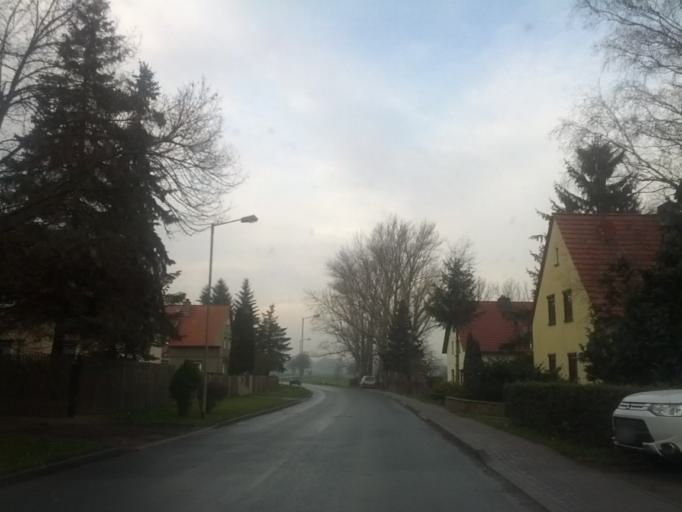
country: DE
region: Thuringia
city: Goldbach
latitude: 50.9950
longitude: 10.6544
